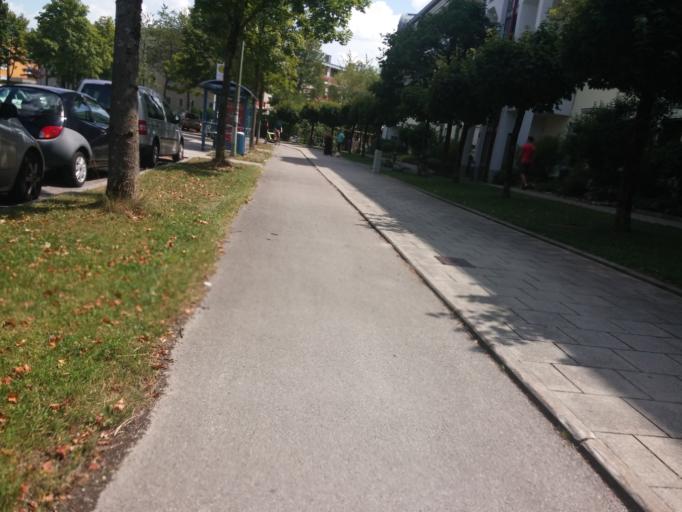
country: DE
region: Bavaria
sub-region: Upper Bavaria
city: Neubiberg
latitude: 48.0863
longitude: 11.6346
